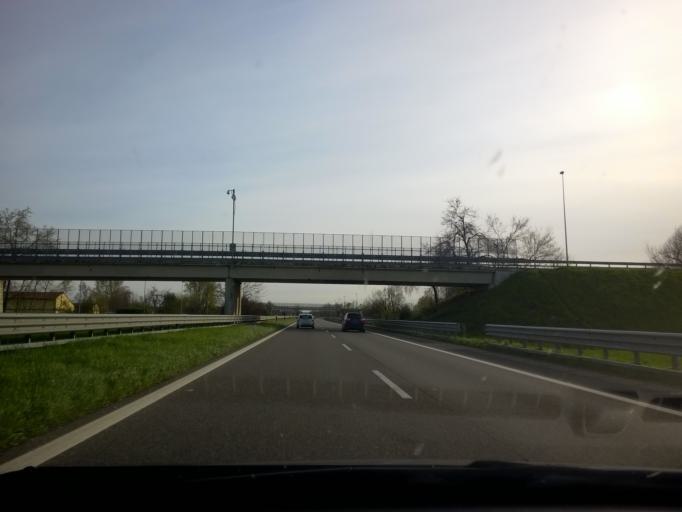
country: IT
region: Lombardy
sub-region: Provincia di Brescia
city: Manerbio
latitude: 45.3650
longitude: 10.1693
